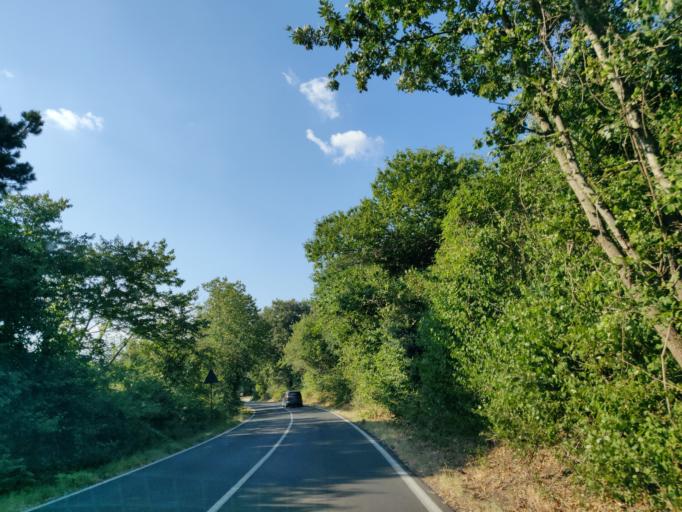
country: IT
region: Latium
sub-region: Provincia di Viterbo
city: Latera
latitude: 42.6282
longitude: 11.8369
